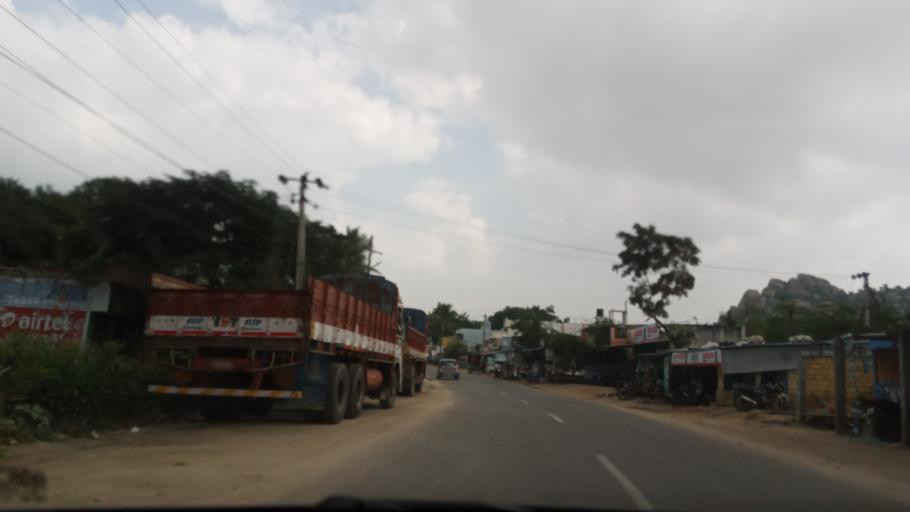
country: IN
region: Andhra Pradesh
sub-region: Chittoor
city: Madanapalle
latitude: 13.6439
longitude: 78.5665
